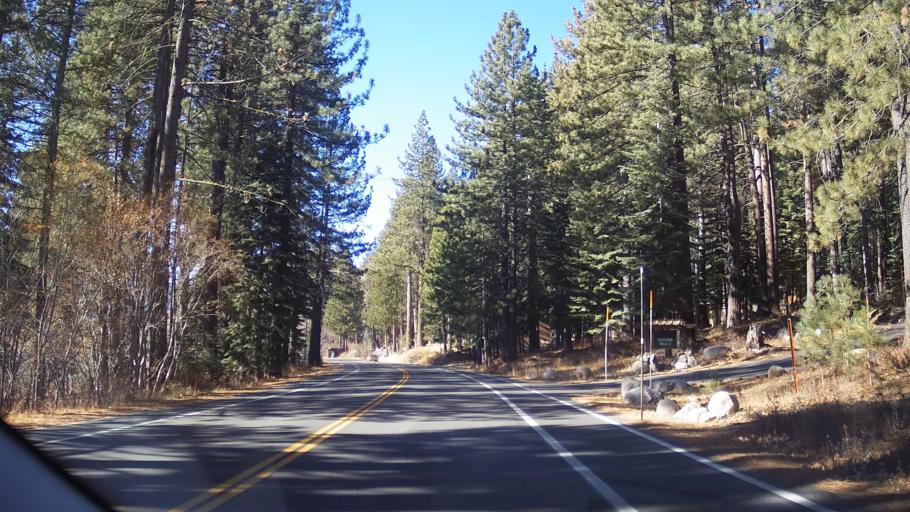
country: US
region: California
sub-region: Nevada County
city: Truckee
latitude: 39.3292
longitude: -120.2552
